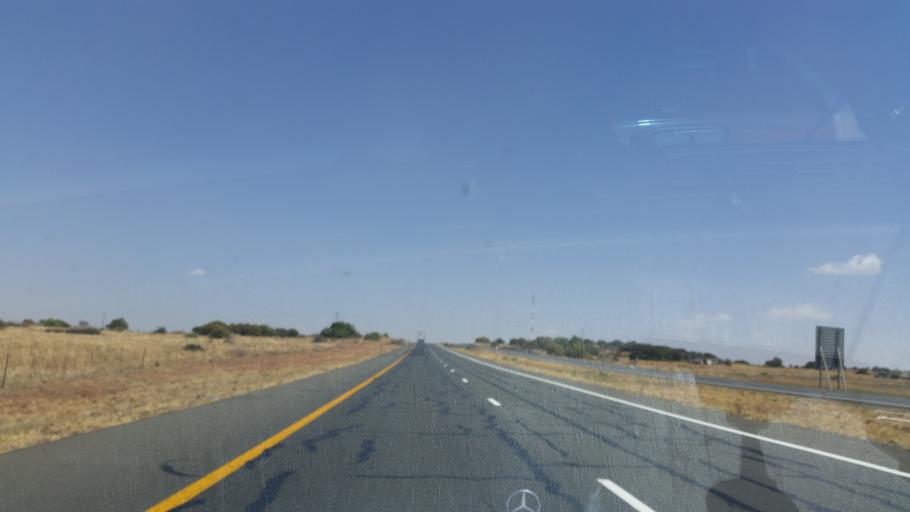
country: ZA
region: Orange Free State
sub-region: Lejweleputswa District Municipality
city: Brandfort
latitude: -28.9046
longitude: 26.4647
